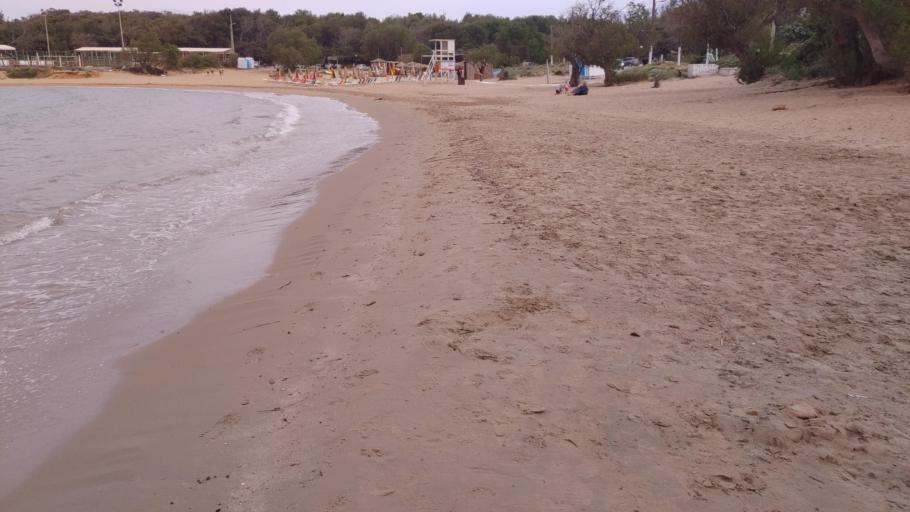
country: GR
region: Crete
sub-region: Nomos Chanias
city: Daratsos
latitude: 35.5147
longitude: 23.9776
